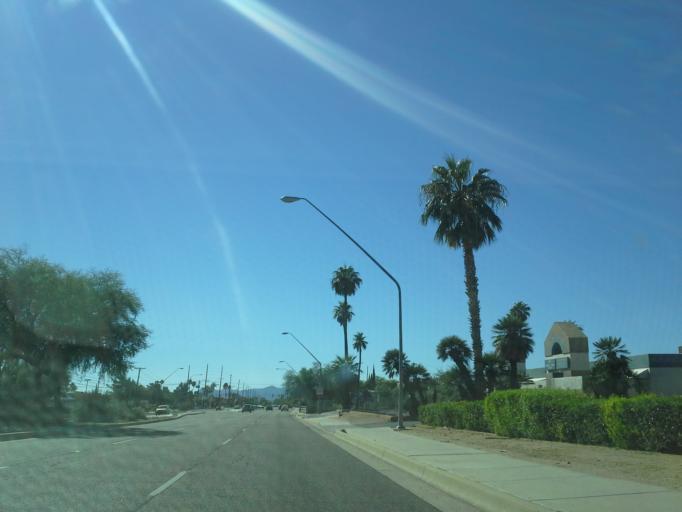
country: US
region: Arizona
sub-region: Pima County
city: Tucson
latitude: 32.2508
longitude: -110.8716
